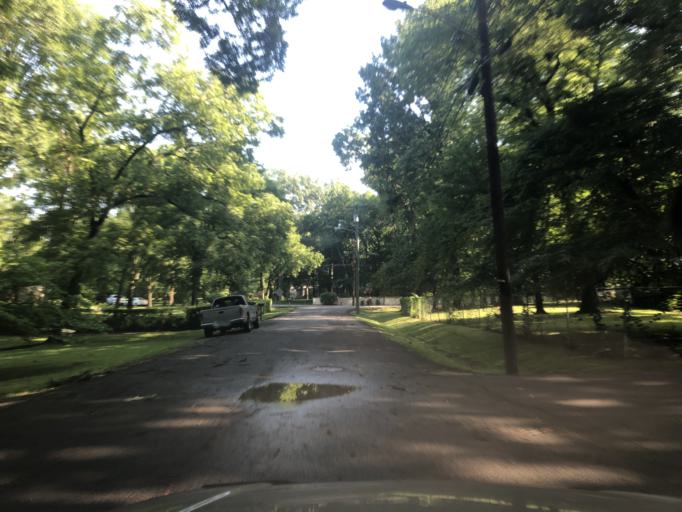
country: US
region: Tennessee
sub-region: Davidson County
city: Lakewood
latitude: 36.2271
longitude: -86.7142
